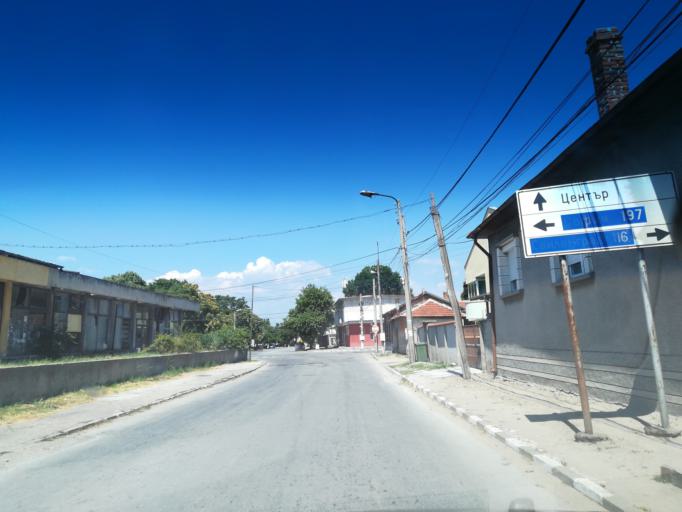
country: BG
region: Stara Zagora
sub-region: Obshtina Chirpan
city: Chirpan
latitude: 42.0766
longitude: 25.1928
